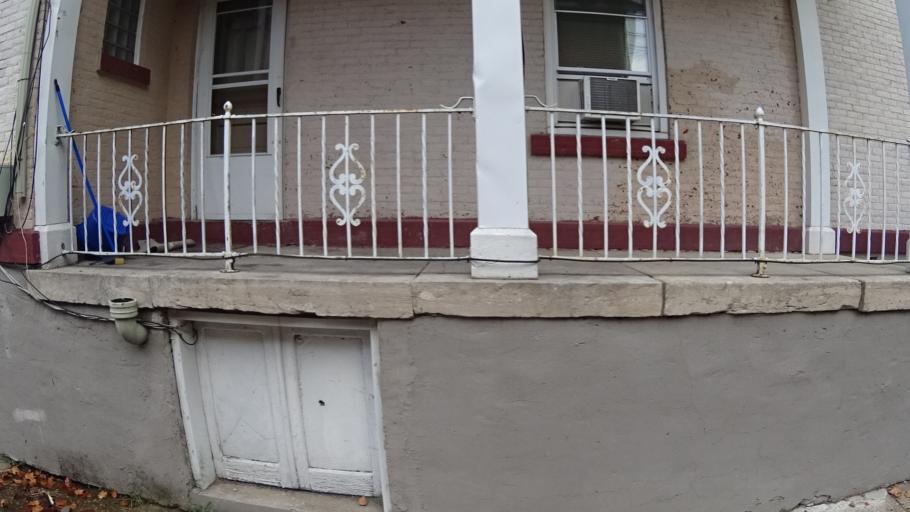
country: US
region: Ohio
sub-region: Erie County
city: Sandusky
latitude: 41.4522
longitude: -82.7197
